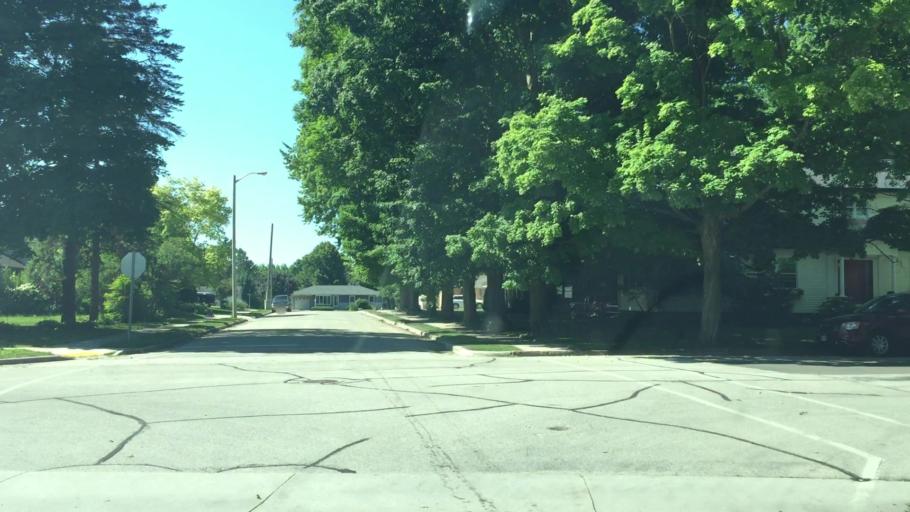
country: US
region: Wisconsin
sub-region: Calumet County
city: New Holstein
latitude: 43.9488
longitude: -88.0958
